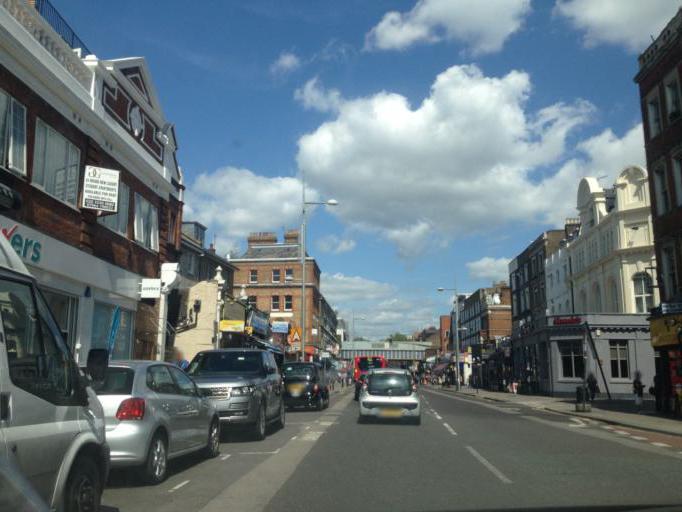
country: GB
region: England
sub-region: Greater London
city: Belsize Park
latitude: 51.5441
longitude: -0.2007
